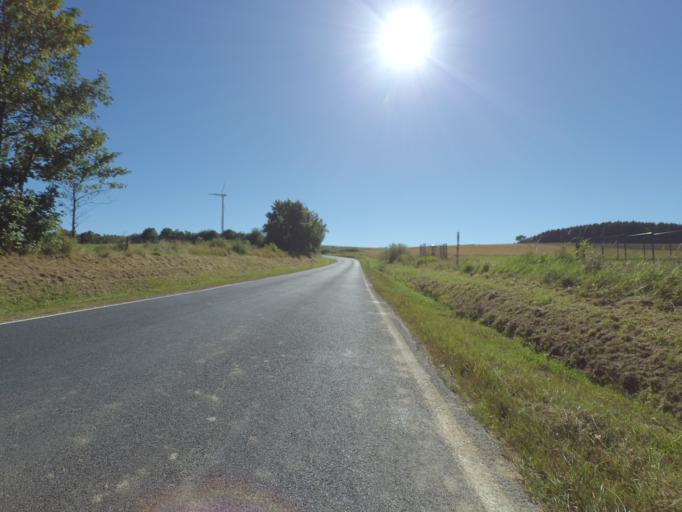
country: DE
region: Rheinland-Pfalz
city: Neichen
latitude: 50.2822
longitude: 6.8684
